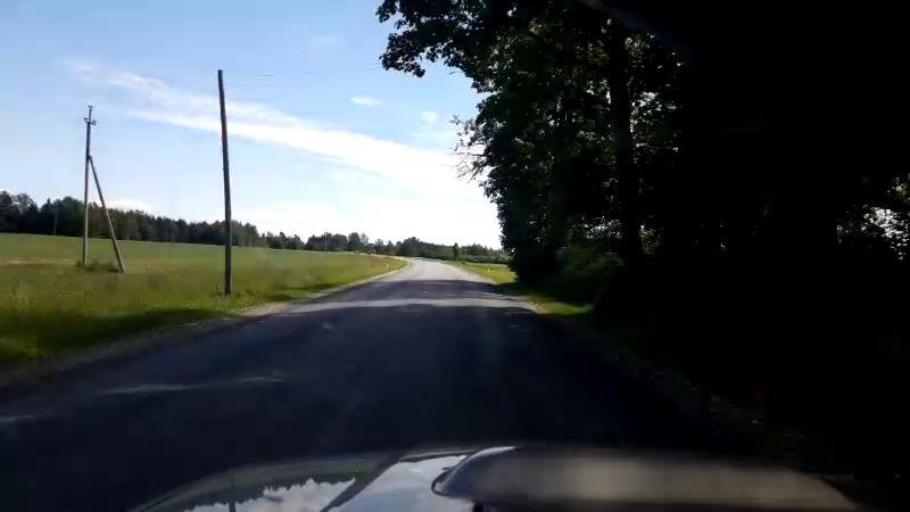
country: EE
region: Laeaene-Virumaa
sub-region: Rakke vald
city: Rakke
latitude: 58.8887
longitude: 26.2868
